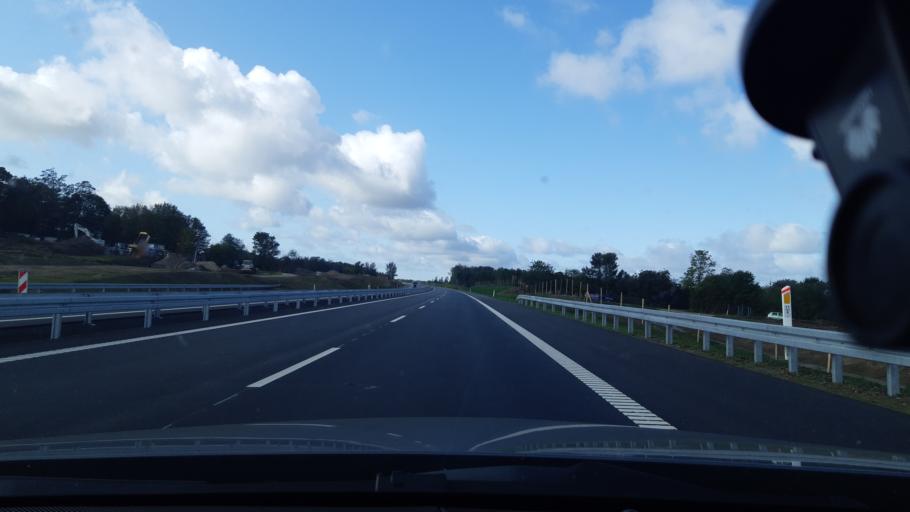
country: DK
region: Zealand
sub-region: Soro Kommune
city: Stenlille
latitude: 55.6614
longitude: 11.5960
